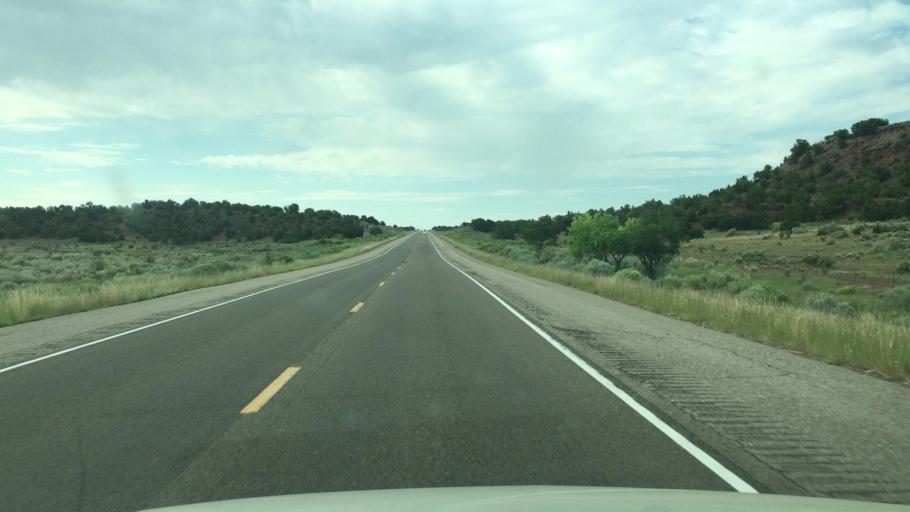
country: US
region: New Mexico
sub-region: Santa Fe County
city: Eldorado at Santa Fe
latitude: 35.2376
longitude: -105.8047
